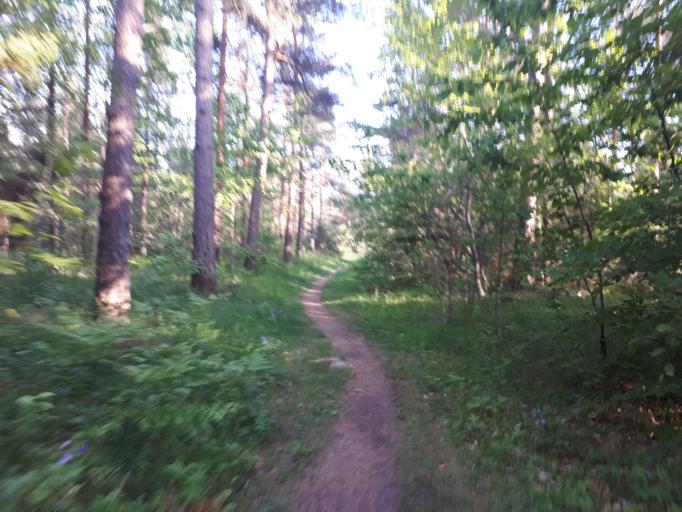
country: SE
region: Gotland
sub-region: Gotland
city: Visby
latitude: 57.6057
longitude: 18.2976
